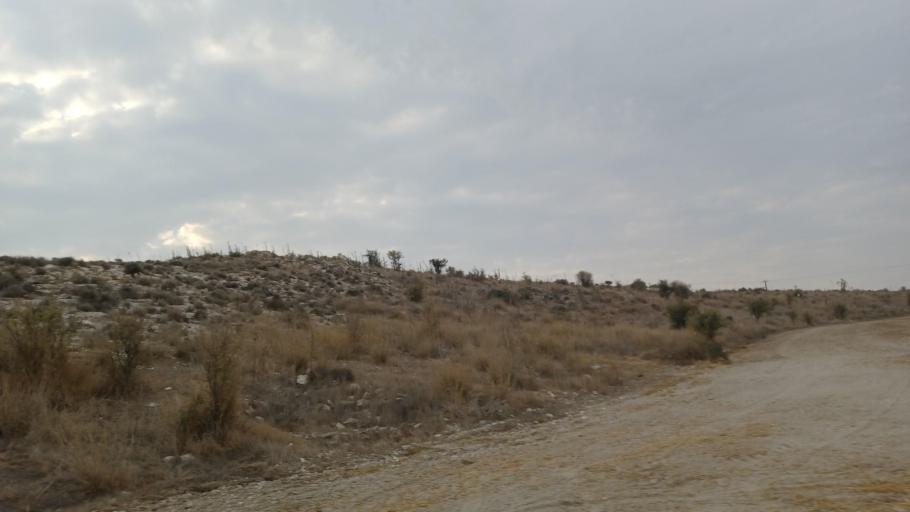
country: CY
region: Larnaka
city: Athienou
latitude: 35.0316
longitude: 33.5718
